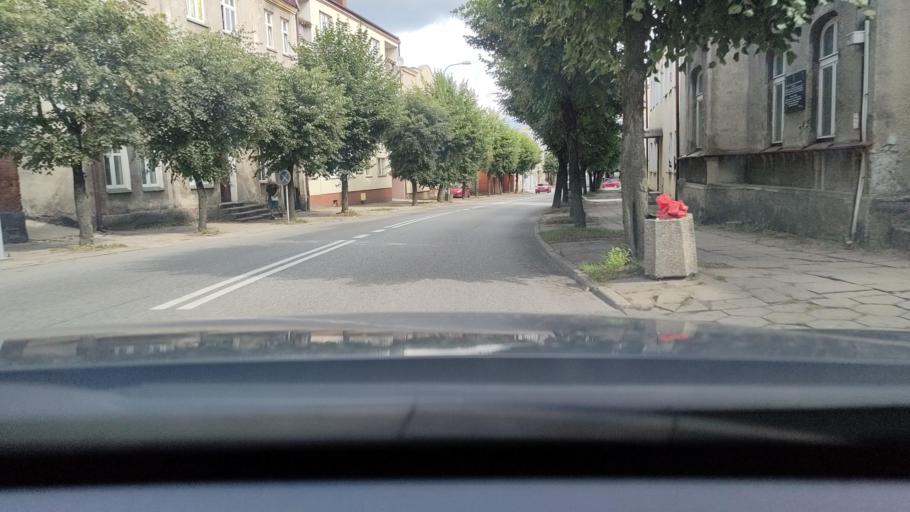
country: PL
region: Pomeranian Voivodeship
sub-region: Powiat wejherowski
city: Wejherowo
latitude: 54.5981
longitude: 18.2321
